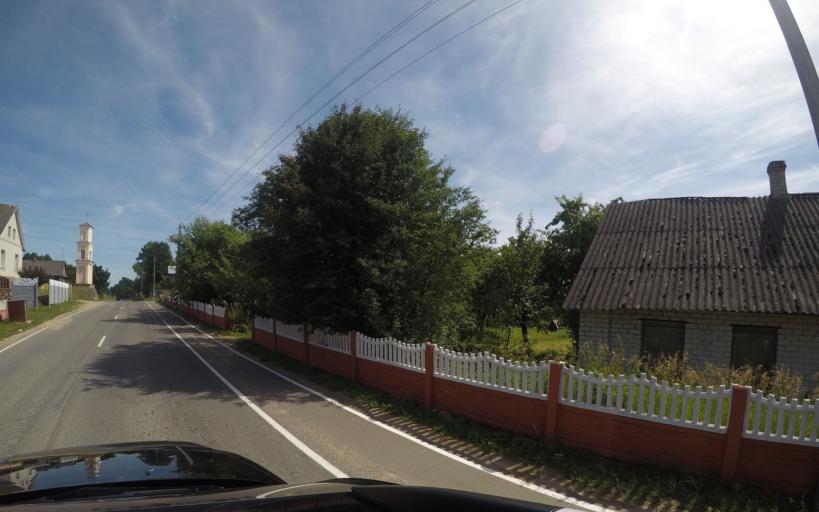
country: BY
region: Grodnenskaya
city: Hal'shany
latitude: 54.2538
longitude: 26.0190
